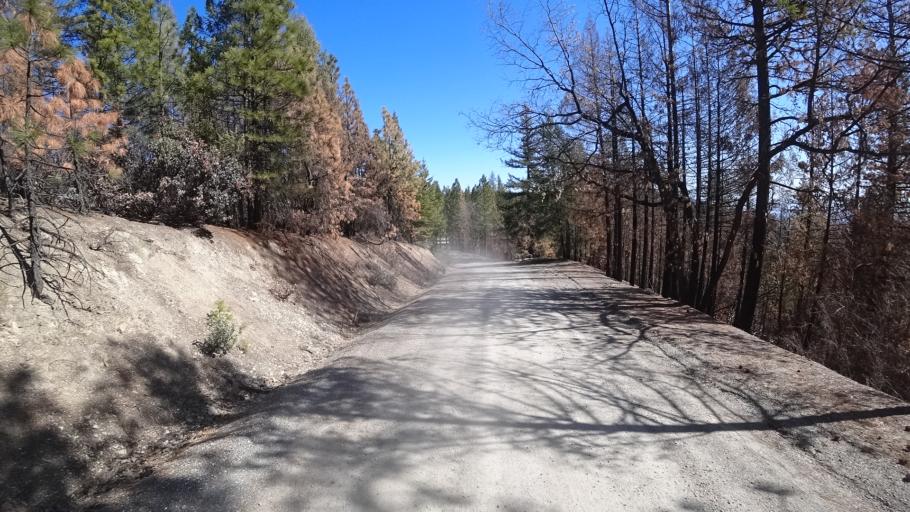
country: US
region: California
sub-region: Tehama County
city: Rancho Tehama Reserve
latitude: 39.6437
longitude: -122.7439
